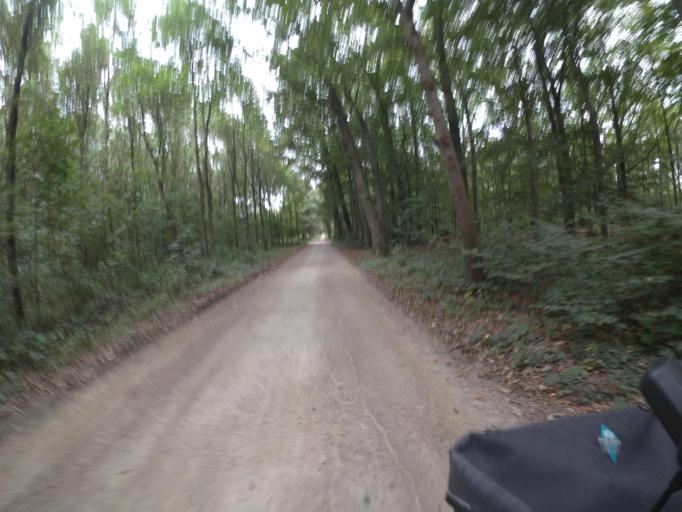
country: BE
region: Flanders
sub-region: Provincie Limburg
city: Sint-Pieters-Voeren
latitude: 50.7580
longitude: 5.7946
